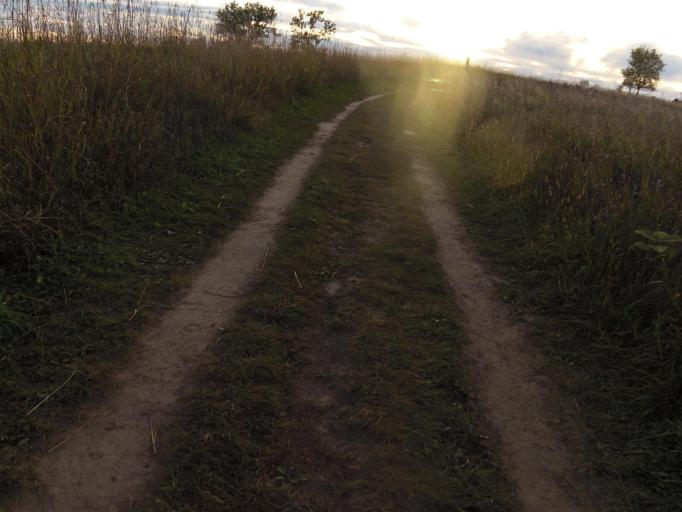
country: US
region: Minnesota
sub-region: Washington County
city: Afton
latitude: 44.8719
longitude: -92.7901
